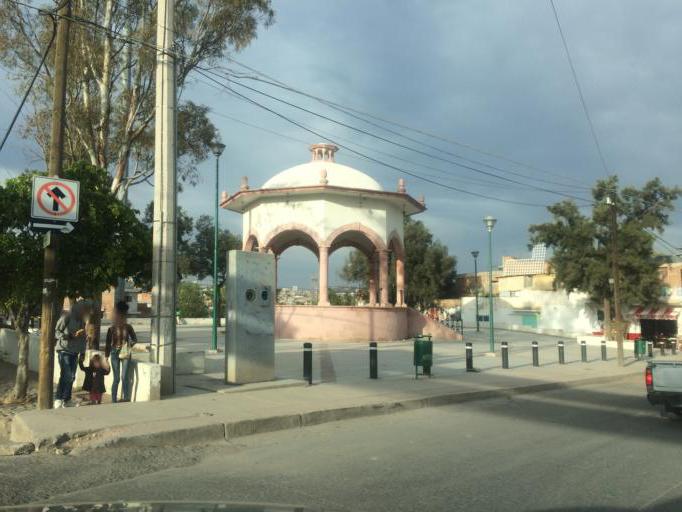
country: MX
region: Guanajuato
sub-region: Leon
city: Centro Familiar la Soledad
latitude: 21.1403
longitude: -101.7483
